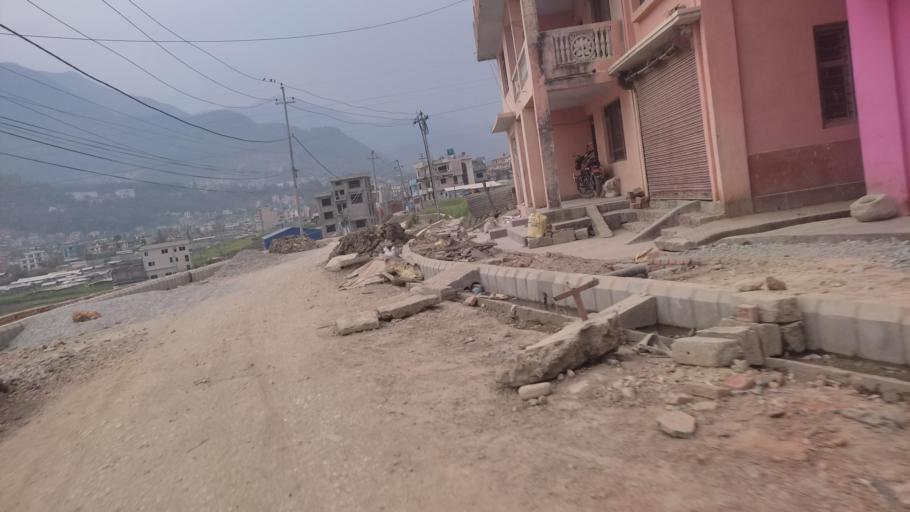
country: NP
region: Central Region
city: Kirtipur
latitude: 27.6632
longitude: 85.2718
